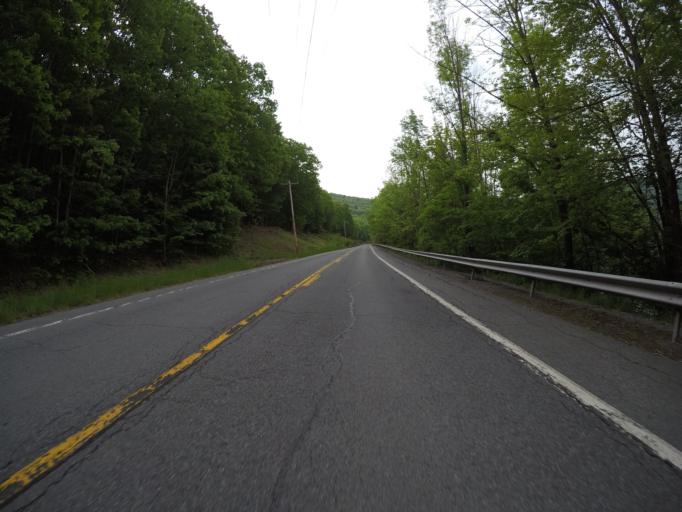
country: US
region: New York
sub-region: Sullivan County
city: Livingston Manor
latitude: 42.0872
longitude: -74.8340
